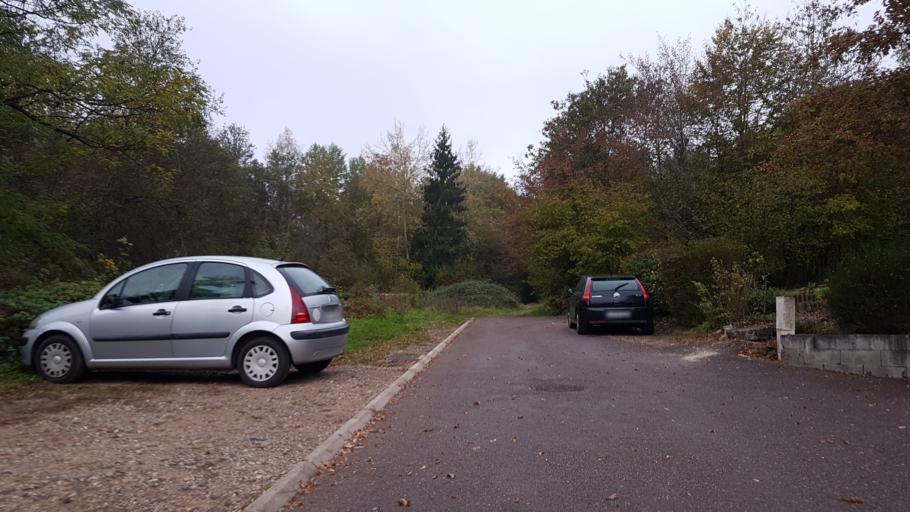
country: FR
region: Franche-Comte
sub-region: Departement de la Haute-Saone
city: Luxeuil-les-Bains
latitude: 47.8270
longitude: 6.3661
